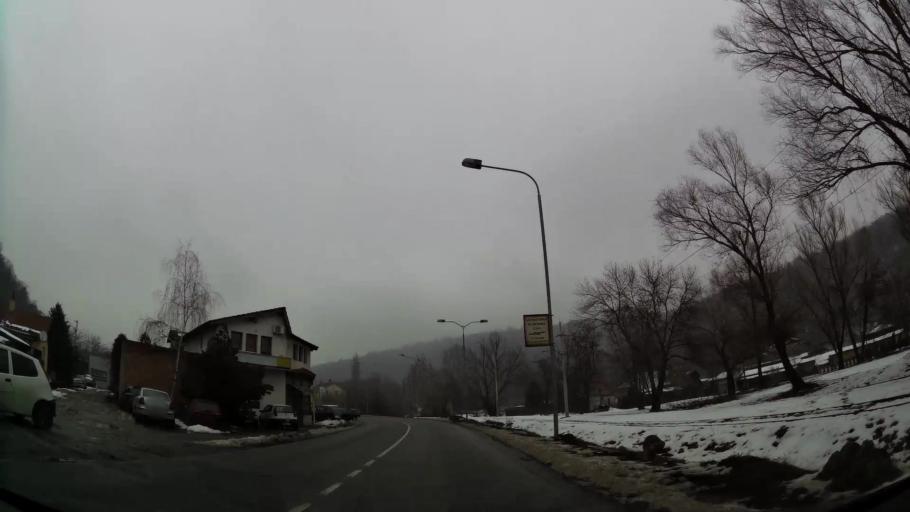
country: RS
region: Central Serbia
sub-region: Belgrade
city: Savski Venac
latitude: 44.7634
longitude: 20.4452
